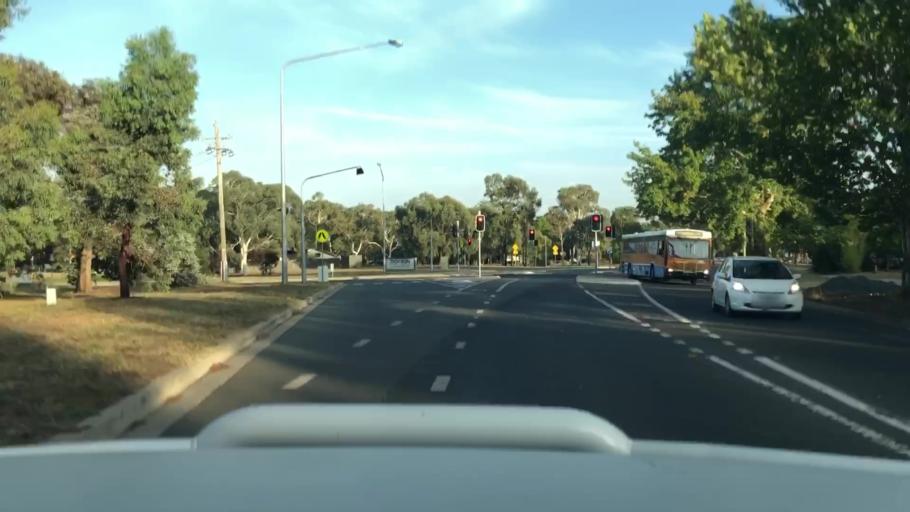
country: AU
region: Australian Capital Territory
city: Canberra
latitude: -35.2507
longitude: 149.1559
